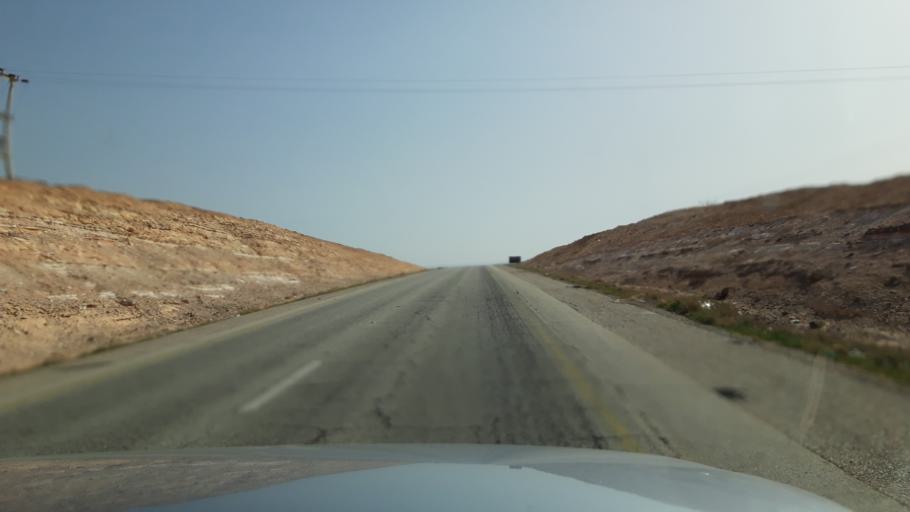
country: JO
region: Amman
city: Al Azraq ash Shamali
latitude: 31.8523
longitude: 36.6784
